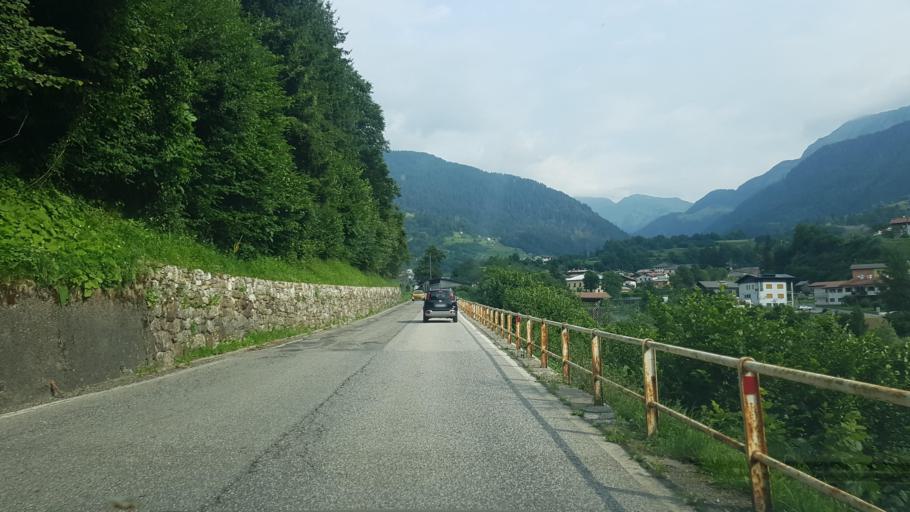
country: IT
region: Friuli Venezia Giulia
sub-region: Provincia di Udine
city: Paularo
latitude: 46.5240
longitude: 13.1214
